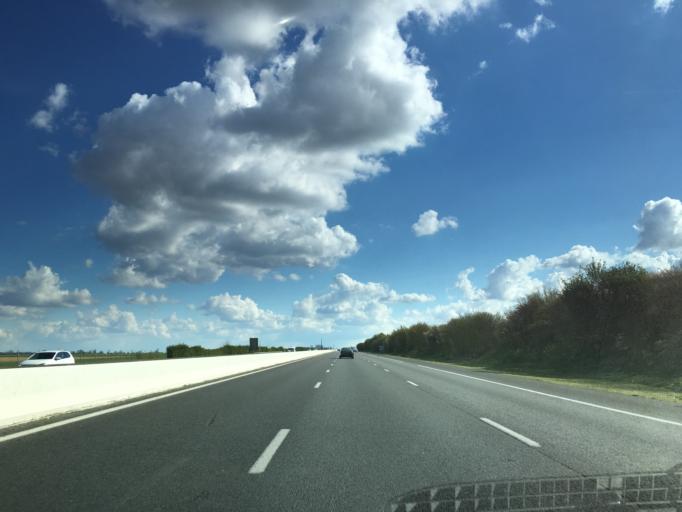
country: FR
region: Nord-Pas-de-Calais
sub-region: Departement du Pas-de-Calais
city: Bapaume
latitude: 50.1221
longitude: 2.8715
